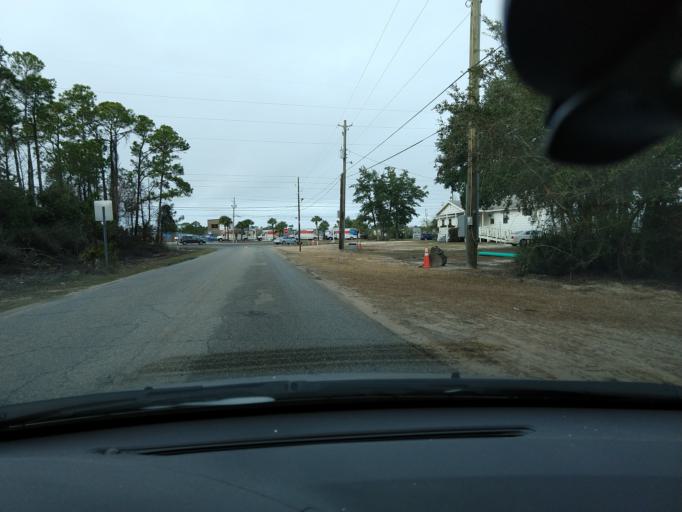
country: US
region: Florida
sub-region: Santa Rosa County
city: Woodlawn Beach
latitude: 30.3993
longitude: -86.9966
